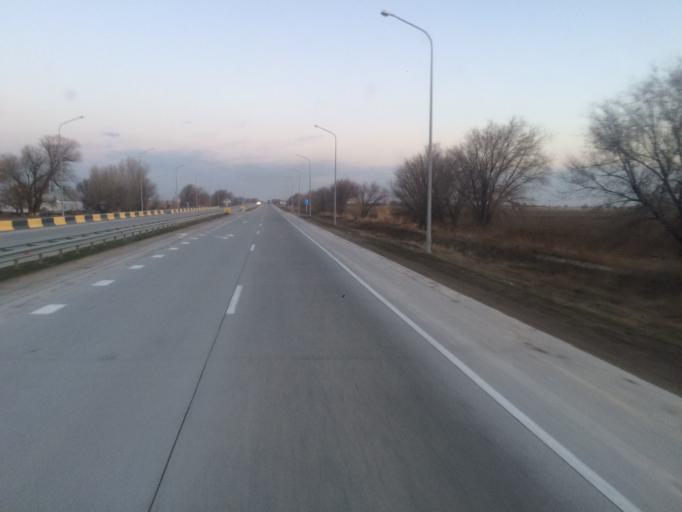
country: KZ
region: Ongtustik Qazaqstan
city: Shayan
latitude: 42.9584
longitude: 68.8916
